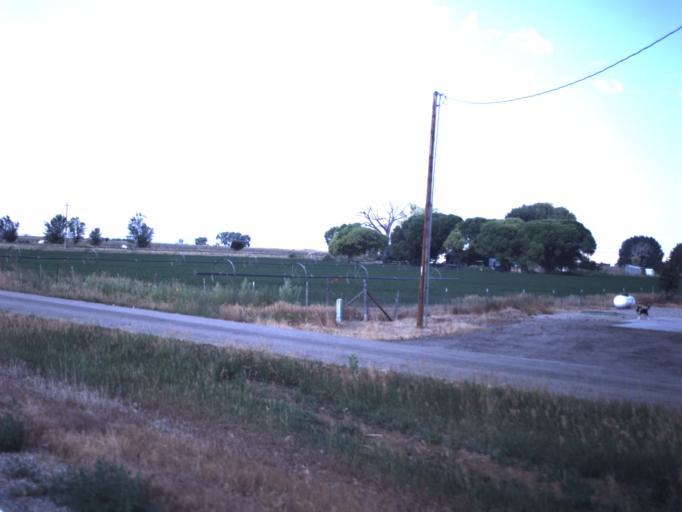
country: US
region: Utah
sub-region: Uintah County
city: Naples
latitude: 40.4002
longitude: -109.3459
